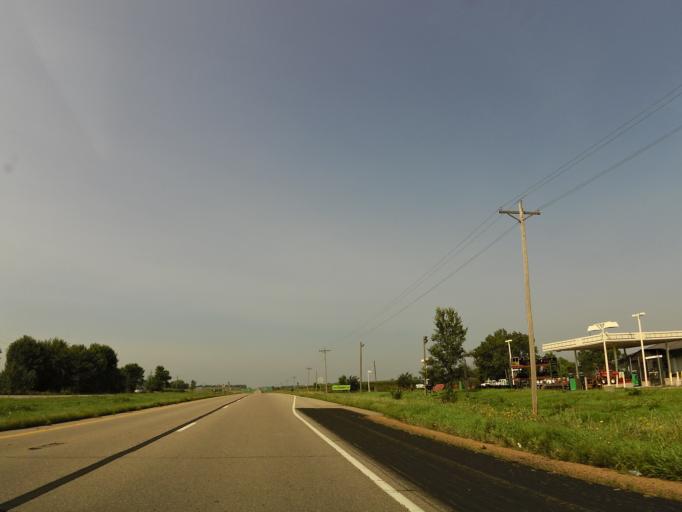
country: US
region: Minnesota
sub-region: Carver County
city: Norwood (historical)
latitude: 44.7683
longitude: -93.9673
